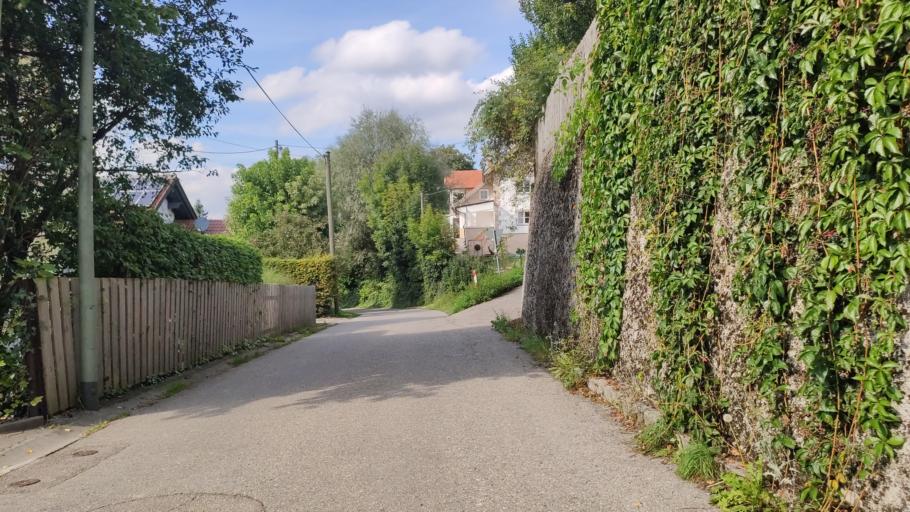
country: DE
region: Bavaria
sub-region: Upper Bavaria
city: Kaufering
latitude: 48.0947
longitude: 10.8740
